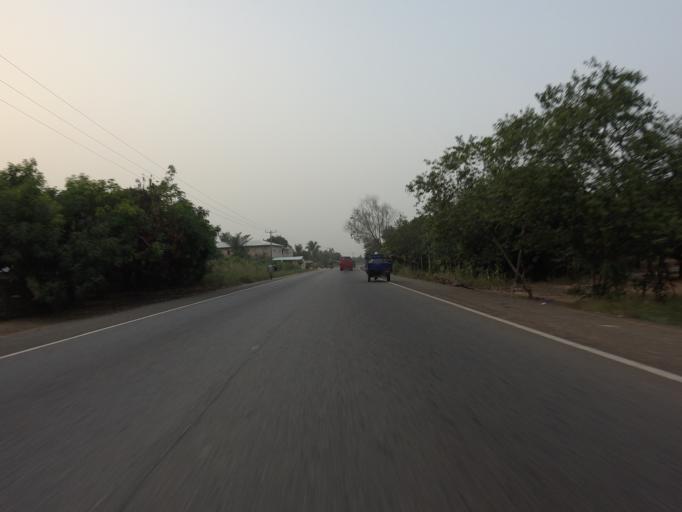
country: GH
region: Volta
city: Anloga
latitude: 5.9941
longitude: 0.5670
